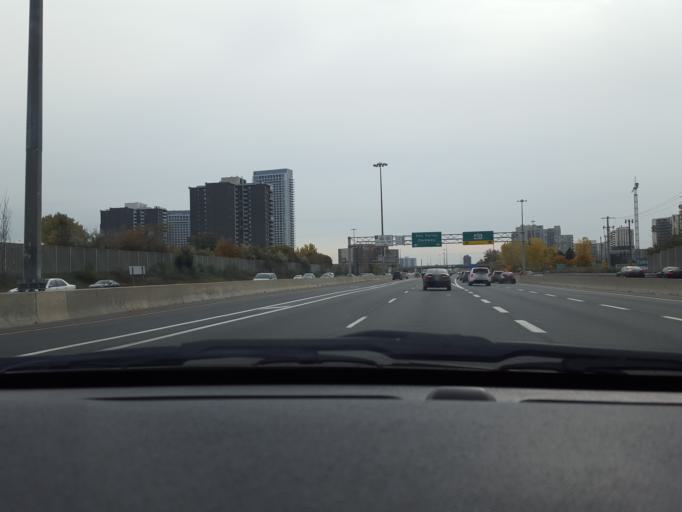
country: CA
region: Ontario
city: Willowdale
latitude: 43.7815
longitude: -79.3408
